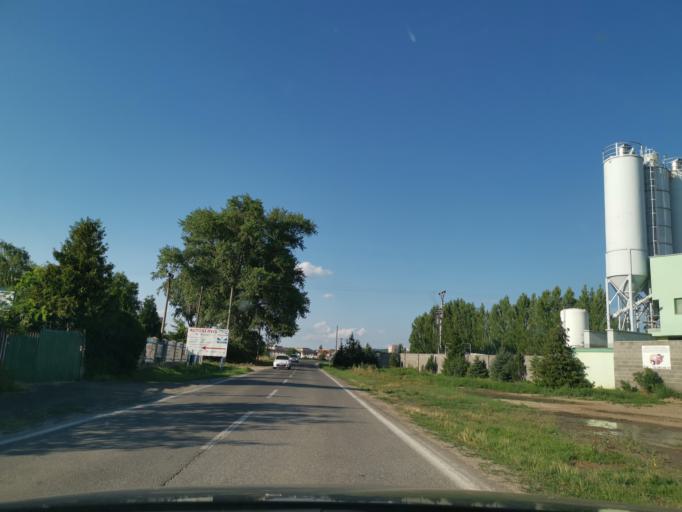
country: SK
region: Bratislavsky
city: Stupava
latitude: 48.2612
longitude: 17.0204
